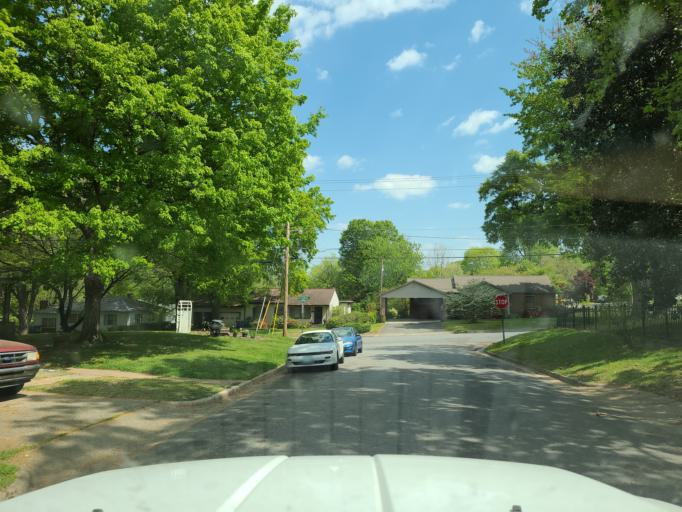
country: US
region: North Carolina
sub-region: Lincoln County
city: Lincolnton
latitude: 35.4750
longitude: -81.2617
